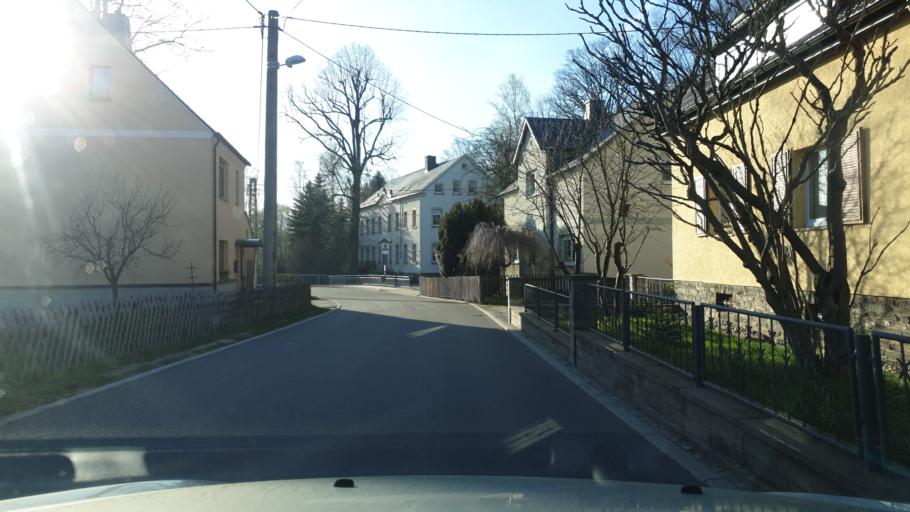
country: DE
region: Saxony
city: Kirchberg
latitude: 50.7624
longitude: 12.7416
